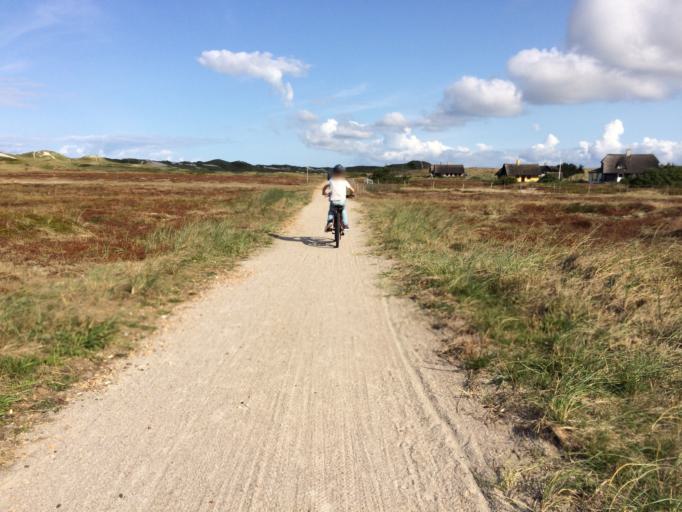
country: DK
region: Central Jutland
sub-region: Ringkobing-Skjern Kommune
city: Hvide Sande
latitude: 55.9050
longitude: 8.1570
